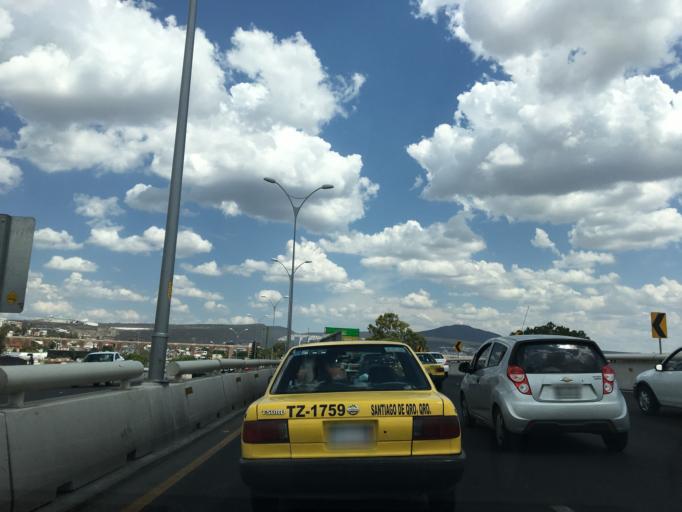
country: MX
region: Queretaro
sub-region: Queretaro
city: Santiago de Queretaro
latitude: 20.6006
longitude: -100.3760
